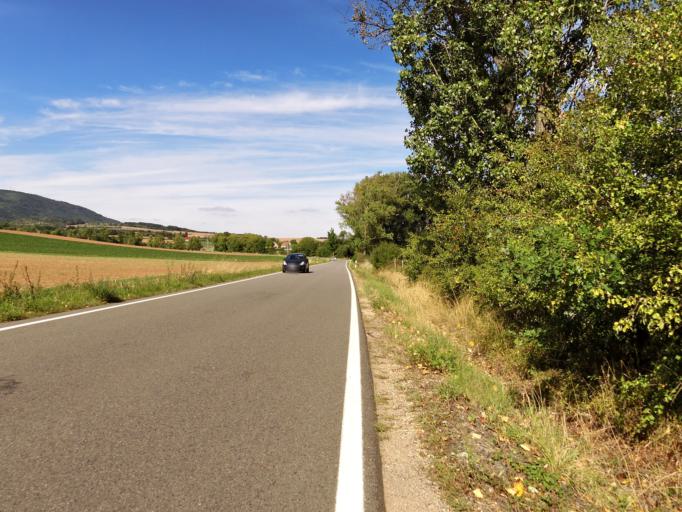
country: DE
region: Rheinland-Pfalz
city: Standenbuhl
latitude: 49.5880
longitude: 7.9723
